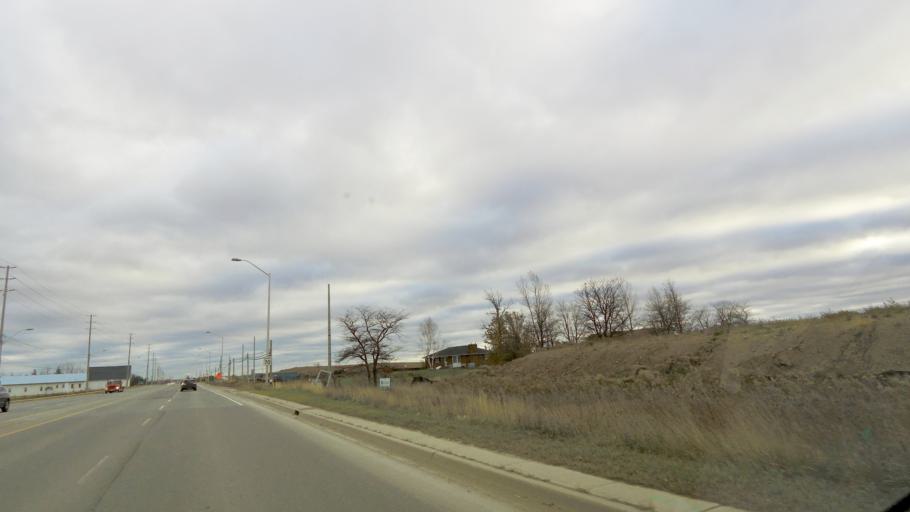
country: CA
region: Ontario
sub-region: Halton
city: Milton
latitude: 43.4961
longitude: -79.8476
